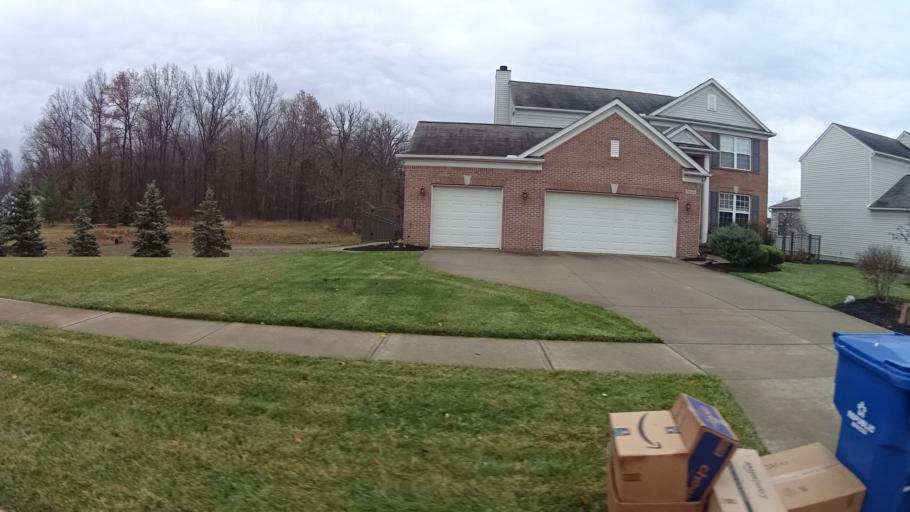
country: US
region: Ohio
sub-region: Lorain County
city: North Ridgeville
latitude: 41.3655
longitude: -82.0517
